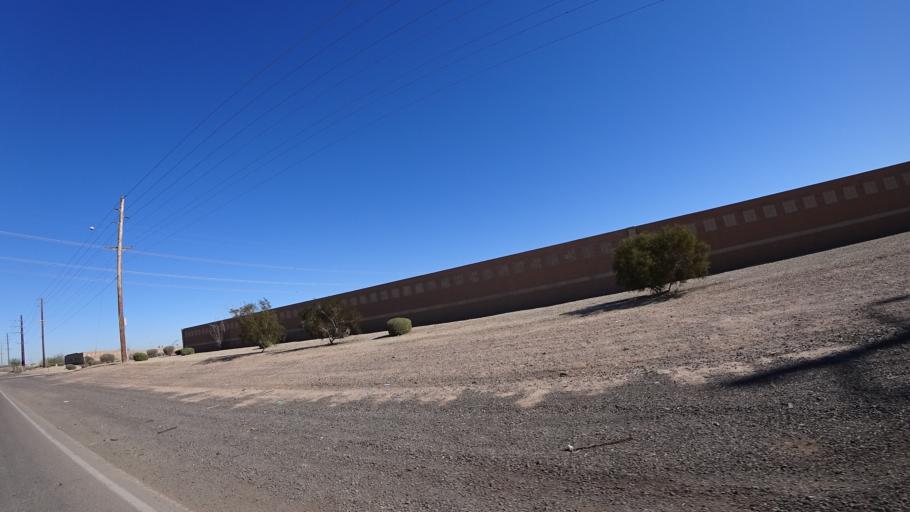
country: US
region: Arizona
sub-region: Maricopa County
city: Tolleson
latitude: 33.3976
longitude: -112.2543
